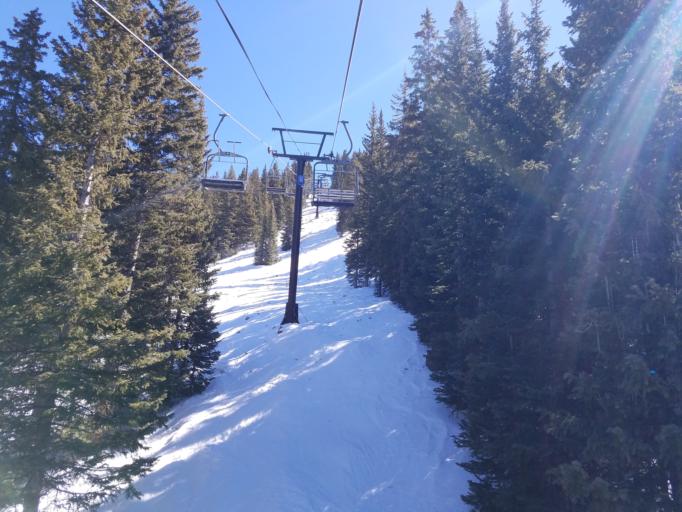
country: US
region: New Mexico
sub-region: Santa Fe County
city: Santa Fe
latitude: 35.7908
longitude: -105.7928
